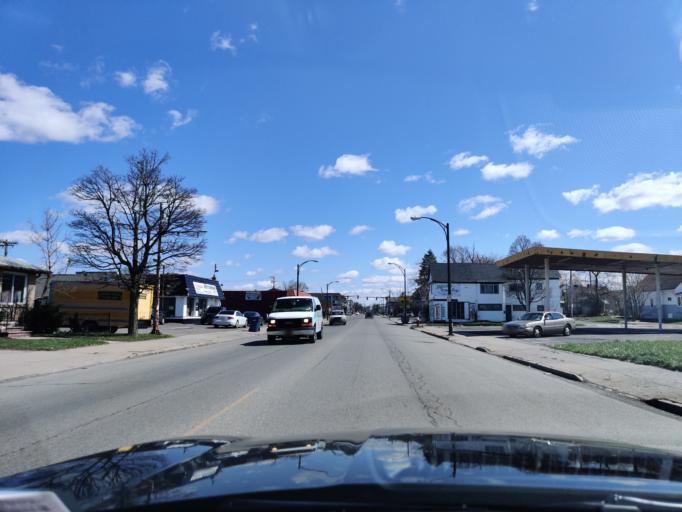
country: US
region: New York
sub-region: Erie County
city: Sloan
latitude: 42.9227
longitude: -78.8122
